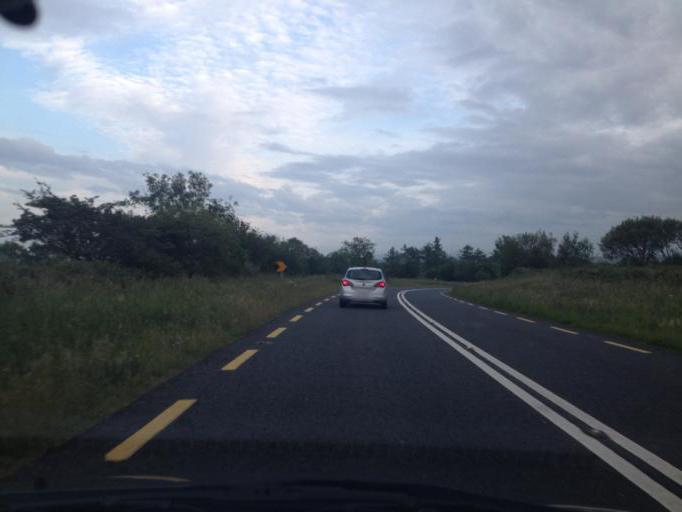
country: IE
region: Connaught
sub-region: Sligo
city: Sligo
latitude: 54.3488
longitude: -8.5045
